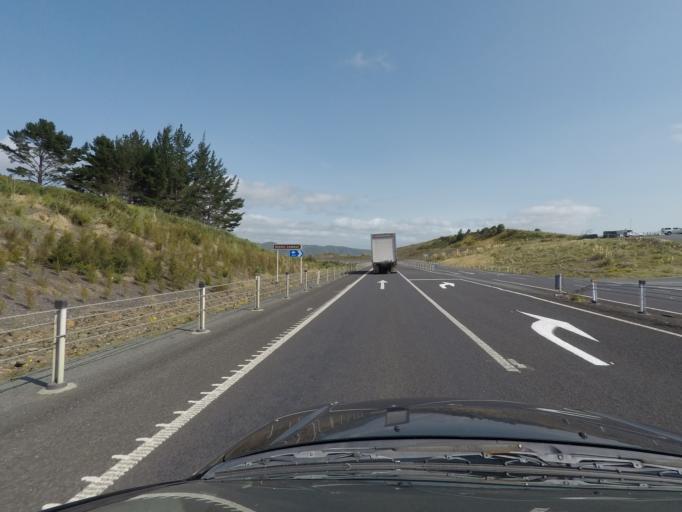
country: NZ
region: Northland
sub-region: Whangarei
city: Ruakaka
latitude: -36.0555
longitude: 174.4255
